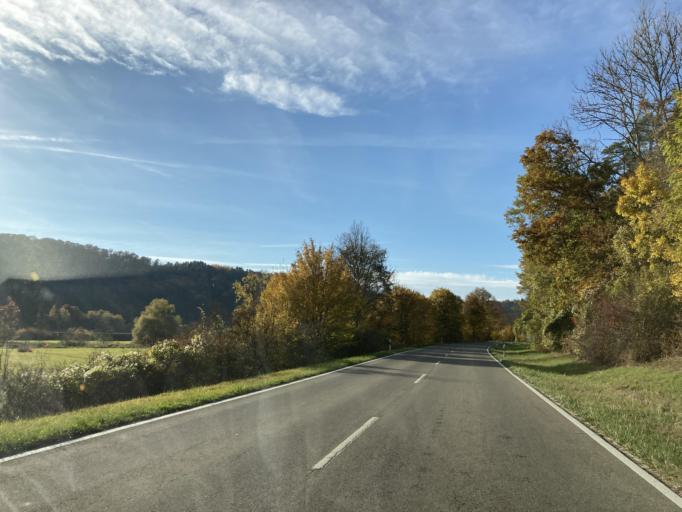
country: DE
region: Baden-Wuerttemberg
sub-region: Karlsruhe Region
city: Horb am Neckar
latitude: 48.4512
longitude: 8.7636
